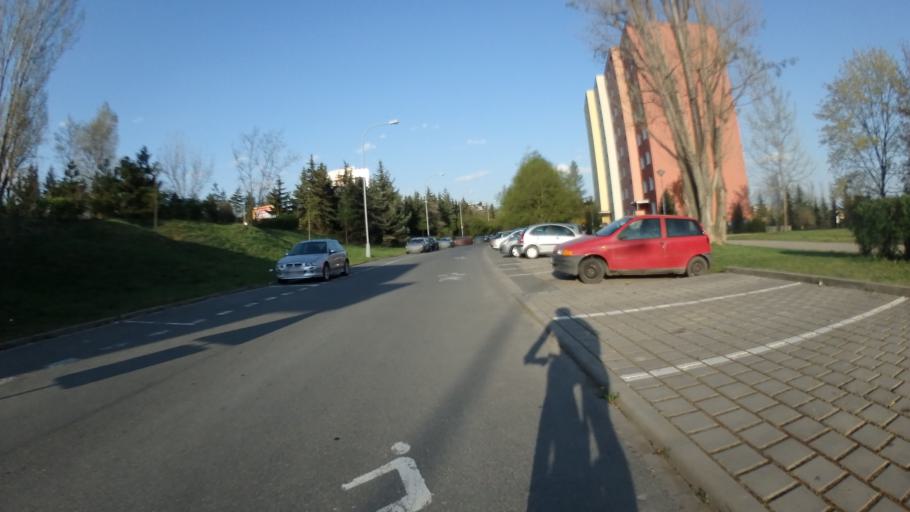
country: CZ
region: South Moravian
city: Moravany
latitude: 49.1730
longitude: 16.5731
